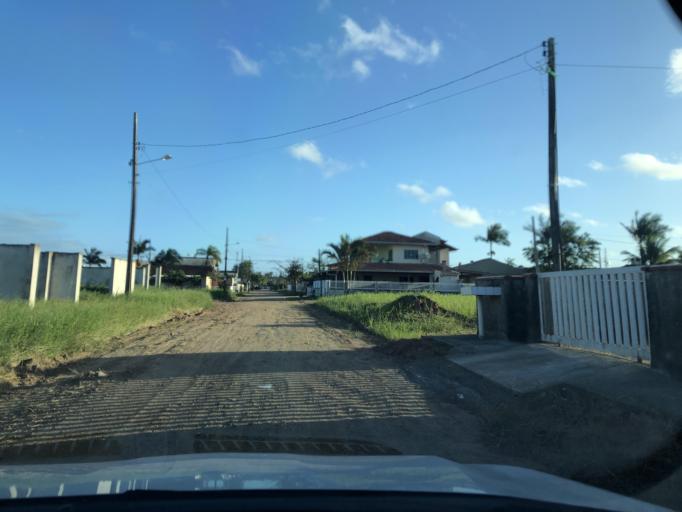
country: BR
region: Santa Catarina
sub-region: Sao Francisco Do Sul
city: Sao Francisco do Sul
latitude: -26.2202
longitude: -48.5272
